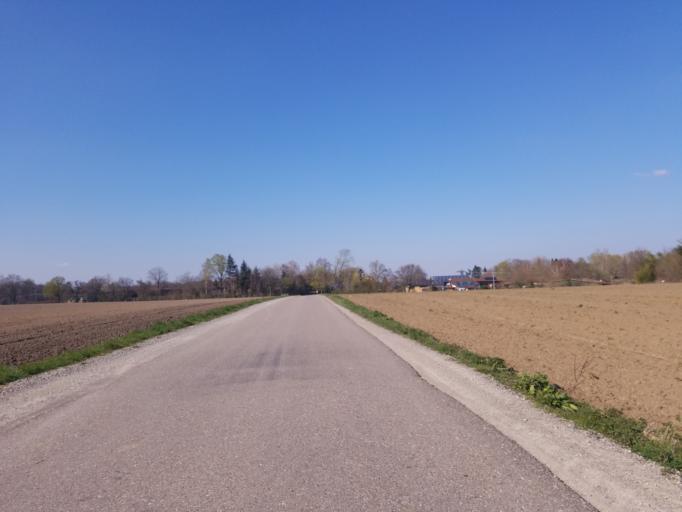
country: DE
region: Baden-Wuerttemberg
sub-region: Karlsruhe Region
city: Schwarzach
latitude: 48.7460
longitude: 8.0614
